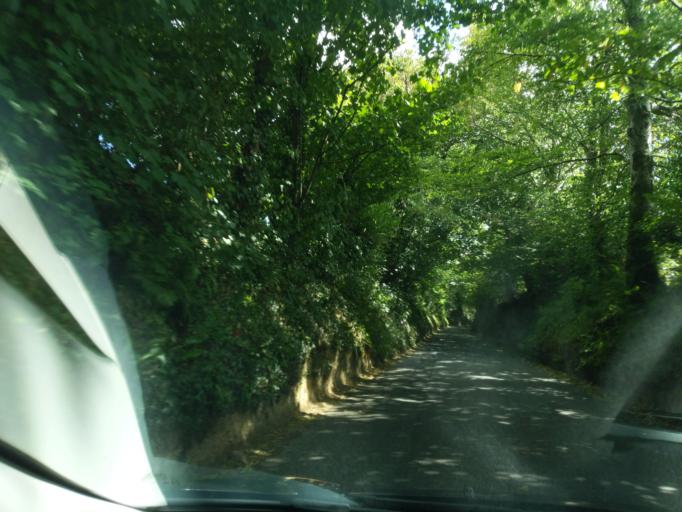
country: GB
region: England
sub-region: Devon
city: Modbury
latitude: 50.3636
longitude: -3.8997
